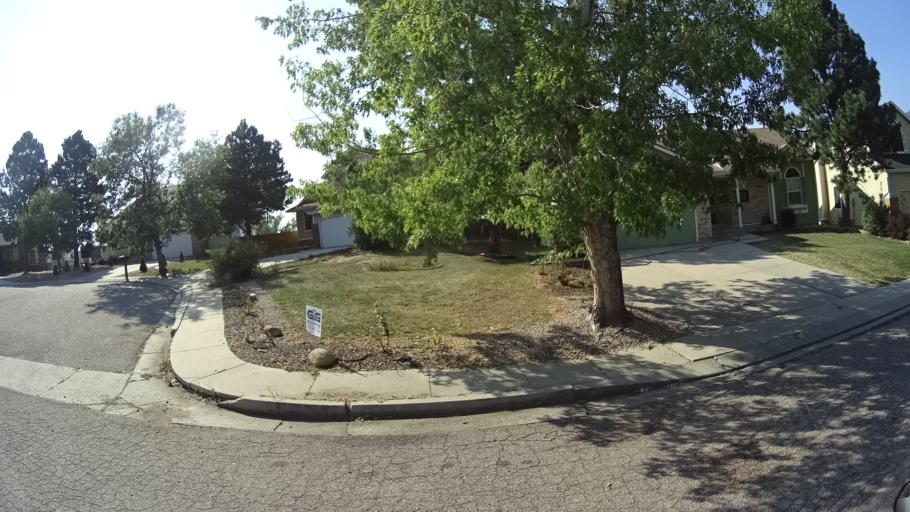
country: US
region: Colorado
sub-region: El Paso County
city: Stratmoor
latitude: 38.7794
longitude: -104.7997
